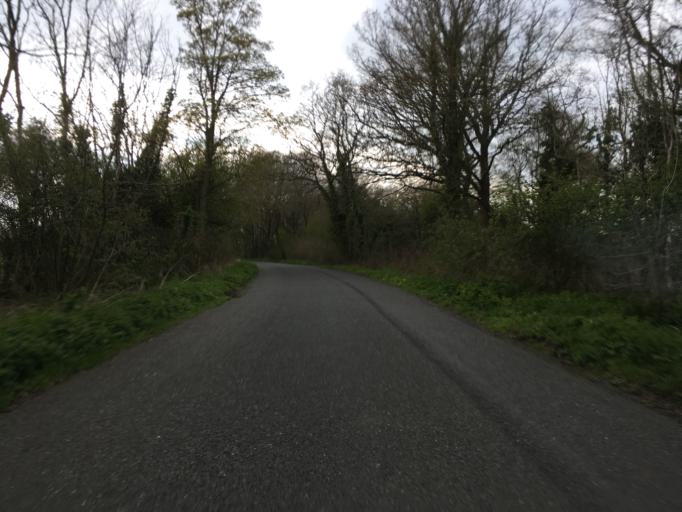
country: GB
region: England
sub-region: Oxfordshire
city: Bicester
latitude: 51.8793
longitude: -1.1773
